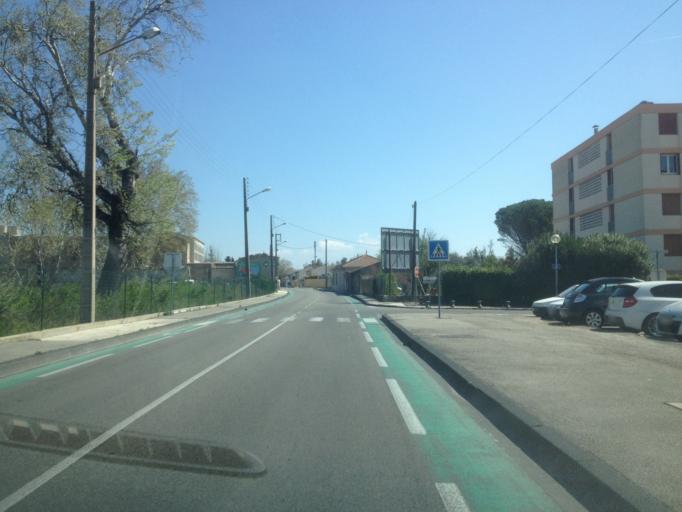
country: FR
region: Provence-Alpes-Cote d'Azur
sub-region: Departement du Vaucluse
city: Le Pontet
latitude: 43.9628
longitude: 4.8667
